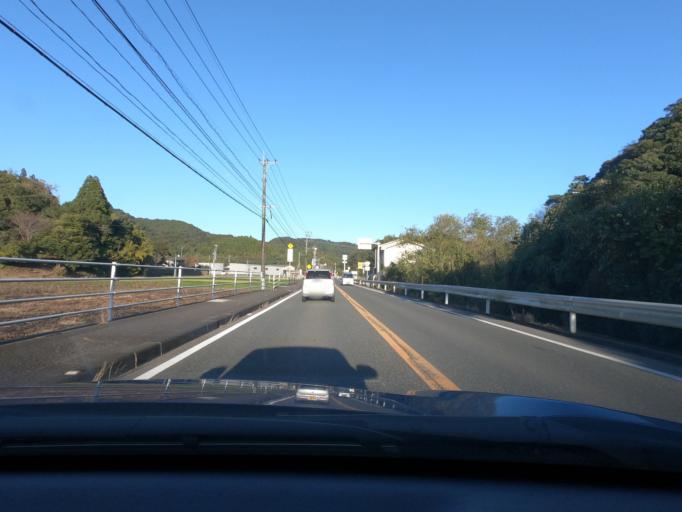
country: JP
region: Kagoshima
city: Satsumasendai
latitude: 31.8485
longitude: 130.2596
